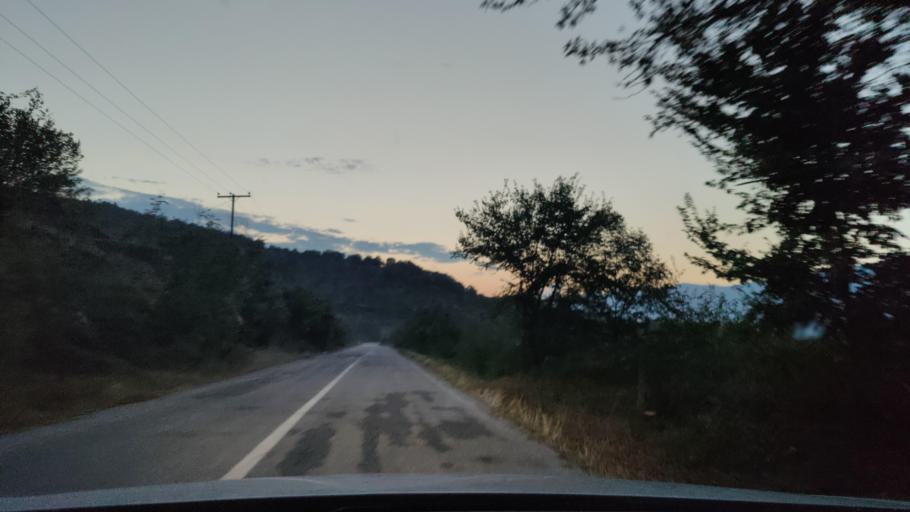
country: GR
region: Central Macedonia
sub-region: Nomos Serron
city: Chrysochorafa
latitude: 41.1990
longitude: 23.0808
